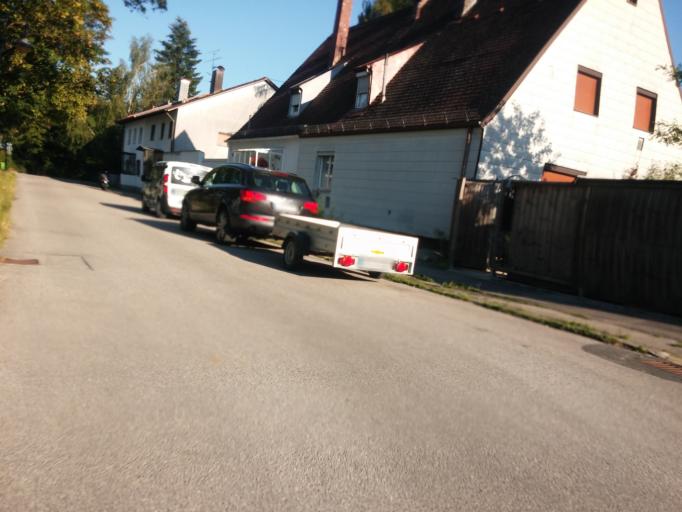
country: DE
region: Bavaria
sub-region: Upper Bavaria
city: Vaterstetten
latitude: 48.1023
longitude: 11.7930
